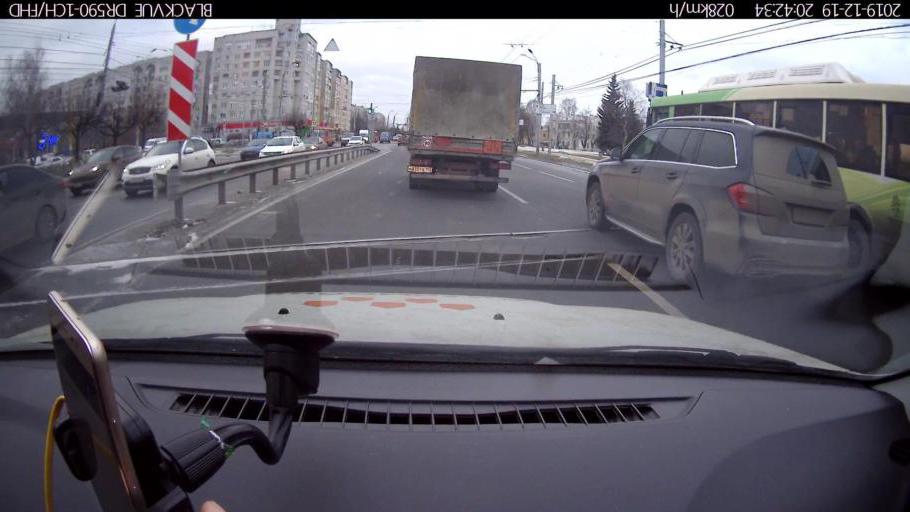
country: RU
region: Nizjnij Novgorod
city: Nizhniy Novgorod
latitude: 56.3238
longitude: 43.8827
